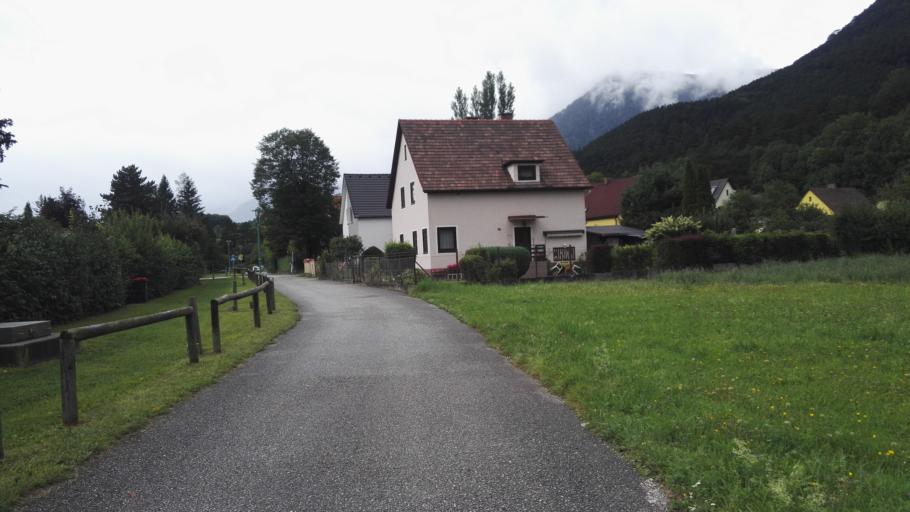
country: AT
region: Lower Austria
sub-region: Politischer Bezirk Neunkirchen
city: Payerbach
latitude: 47.6934
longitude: 15.8705
